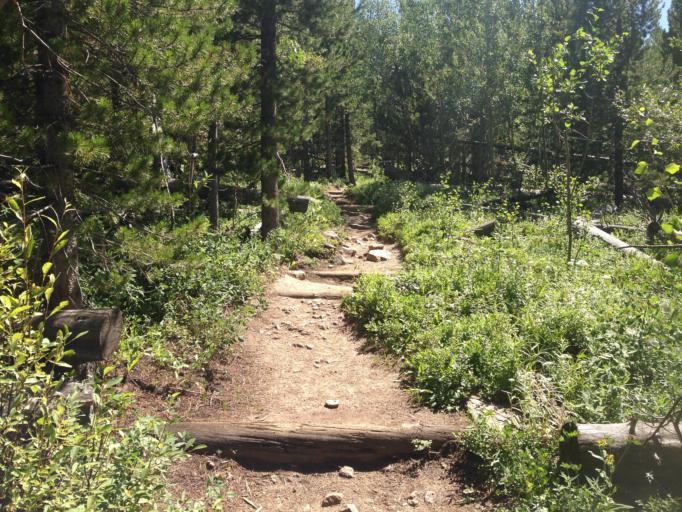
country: US
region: Colorado
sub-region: Larimer County
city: Estes Park
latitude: 40.1958
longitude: -105.5719
